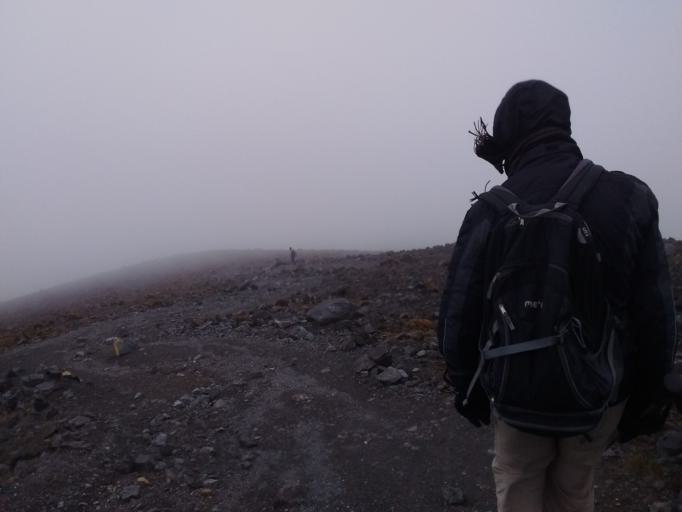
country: CO
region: Cauca
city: Totoro
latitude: 2.3237
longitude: -76.3950
